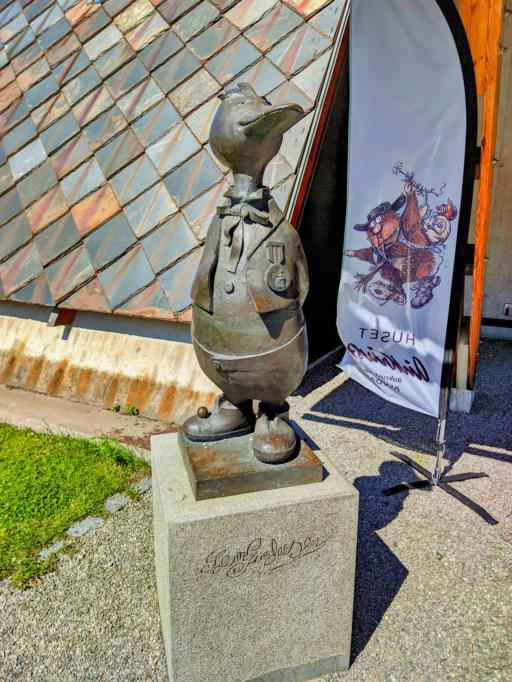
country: NO
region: Hedmark
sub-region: Alvdal
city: Alvdal
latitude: 62.1135
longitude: 10.6220
